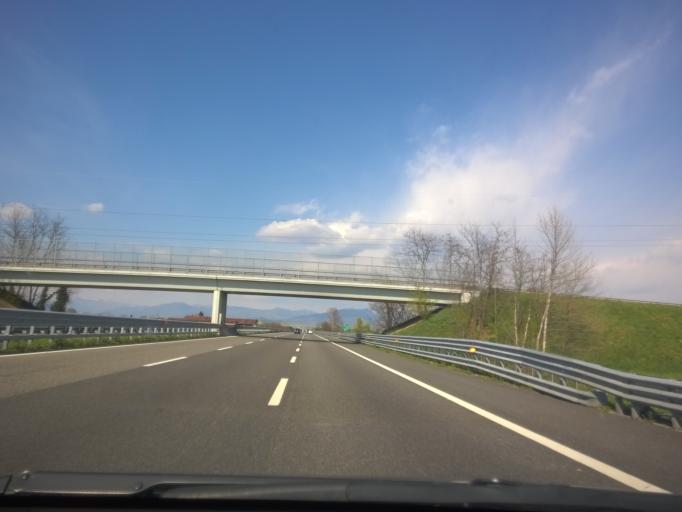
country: IT
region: Lombardy
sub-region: Provincia di Brescia
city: Bagnolo Mella
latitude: 45.4228
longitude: 10.1989
